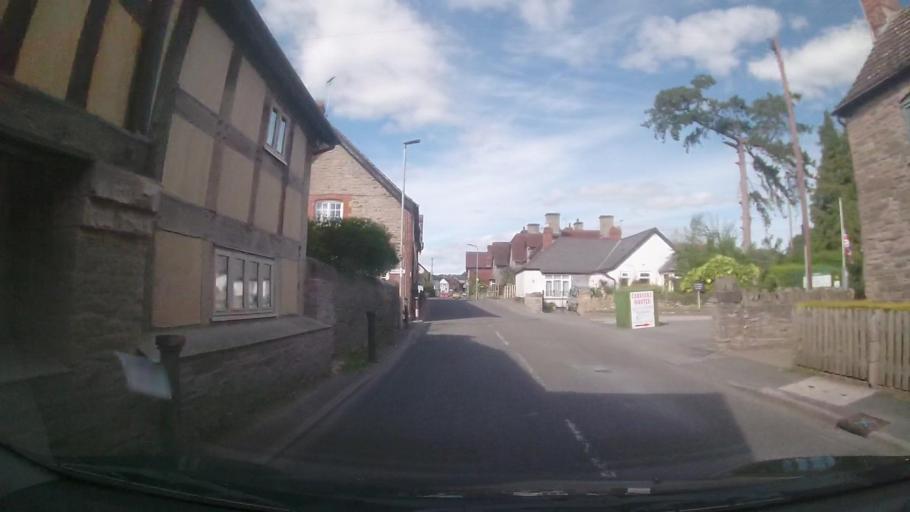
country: GB
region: England
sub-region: Herefordshire
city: Kinnersley
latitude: 52.1390
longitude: -3.0073
